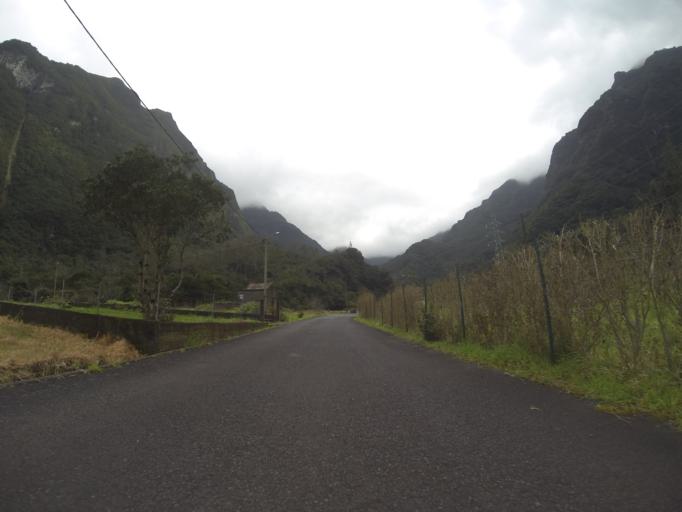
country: PT
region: Madeira
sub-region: Porto Moniz
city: Porto Moniz
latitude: 32.8040
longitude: -17.1153
